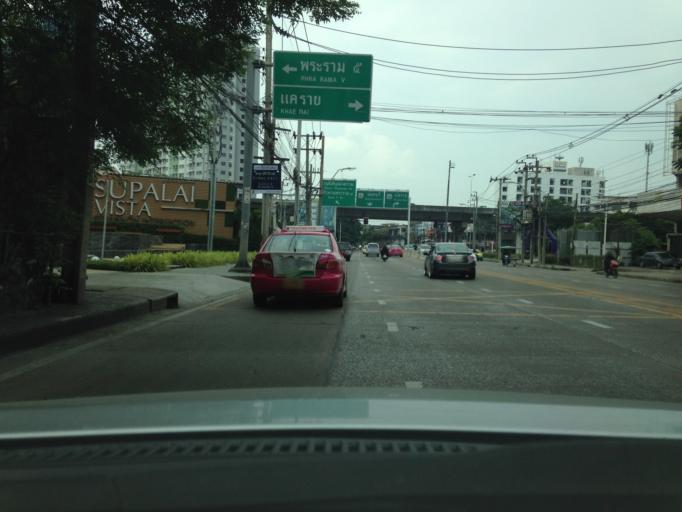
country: TH
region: Nonthaburi
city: Mueang Nonthaburi
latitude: 13.8420
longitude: 100.5119
